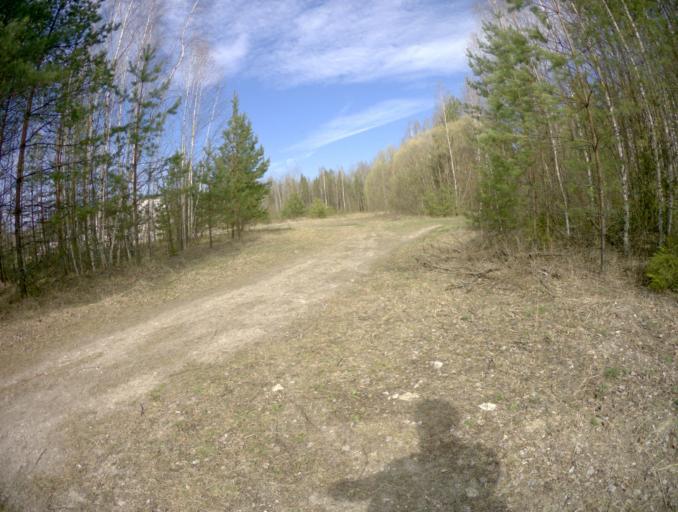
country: RU
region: Vladimir
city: Mezinovskiy
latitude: 55.5081
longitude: 40.2956
